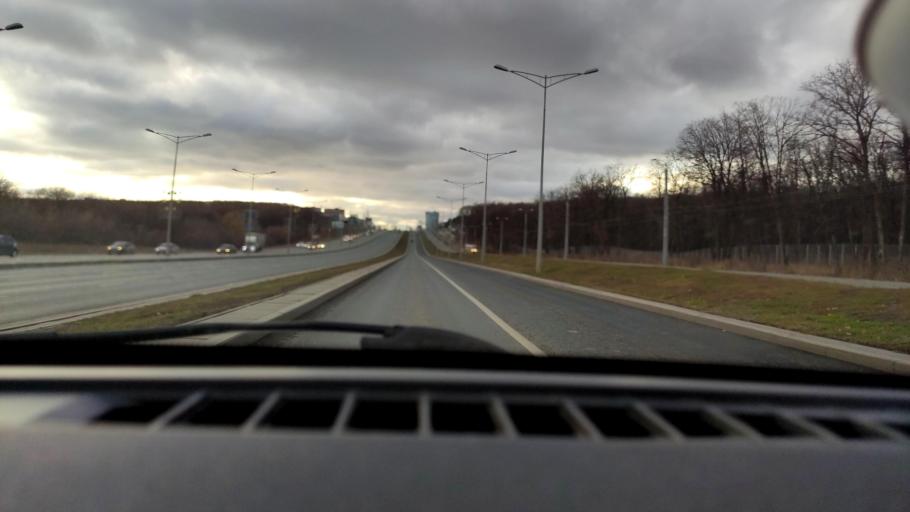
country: RU
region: Samara
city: Petra-Dubrava
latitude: 53.2692
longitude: 50.2532
